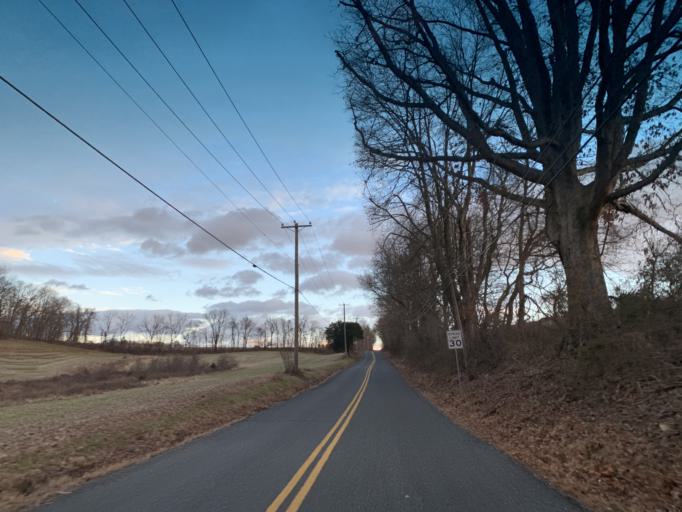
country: US
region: Pennsylvania
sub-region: York County
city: Susquehanna Trails
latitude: 39.6632
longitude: -76.3202
